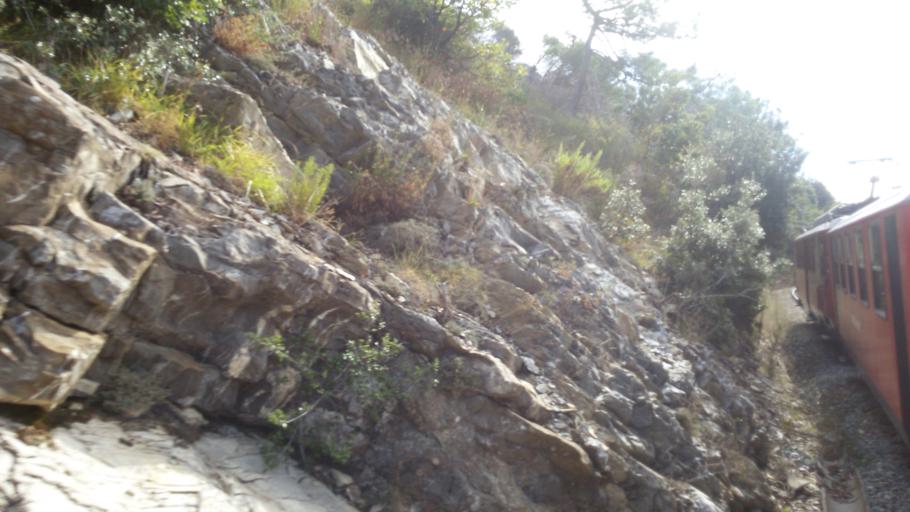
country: IT
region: Liguria
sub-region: Provincia di Genova
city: Genoa
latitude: 44.4402
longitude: 8.9399
